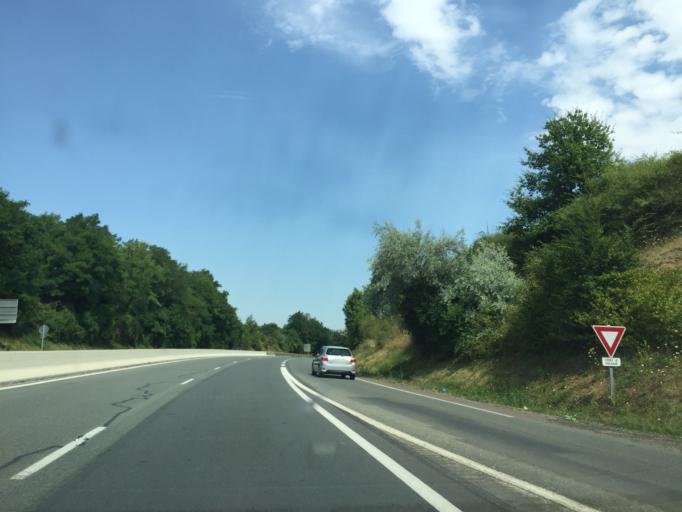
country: FR
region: Poitou-Charentes
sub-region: Departement de la Vienne
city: Biard
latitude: 46.5639
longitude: 0.3032
